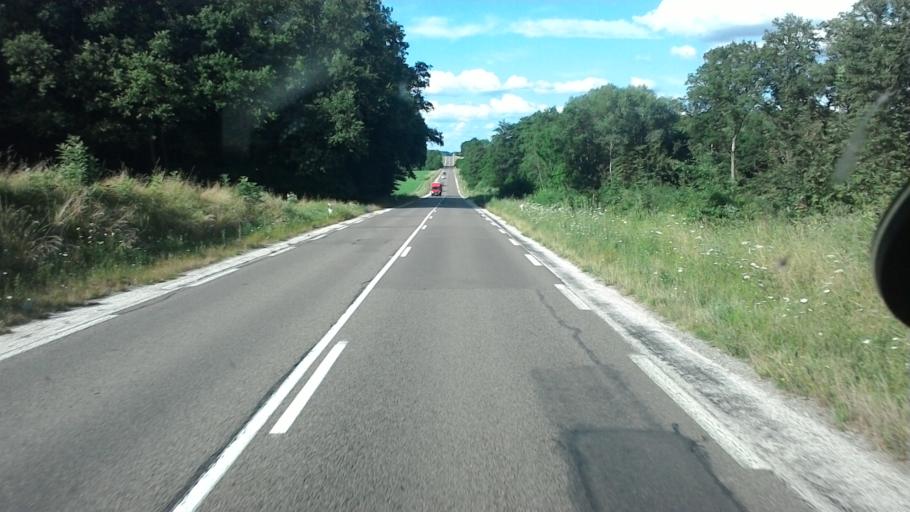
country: FR
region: Franche-Comte
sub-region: Departement de la Haute-Saone
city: Luxeuil-les-Bains
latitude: 47.7089
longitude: 6.2952
